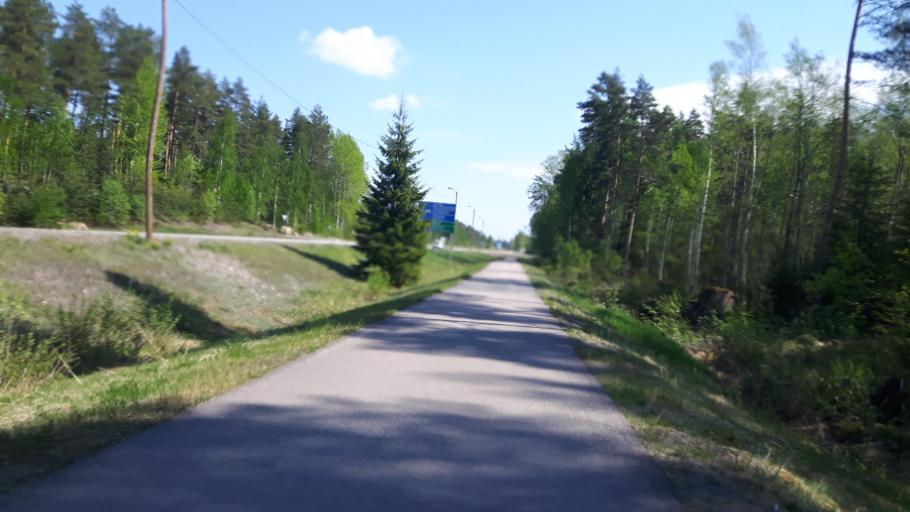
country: FI
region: Uusimaa
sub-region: Loviisa
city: Lovisa
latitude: 60.4653
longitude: 26.2665
